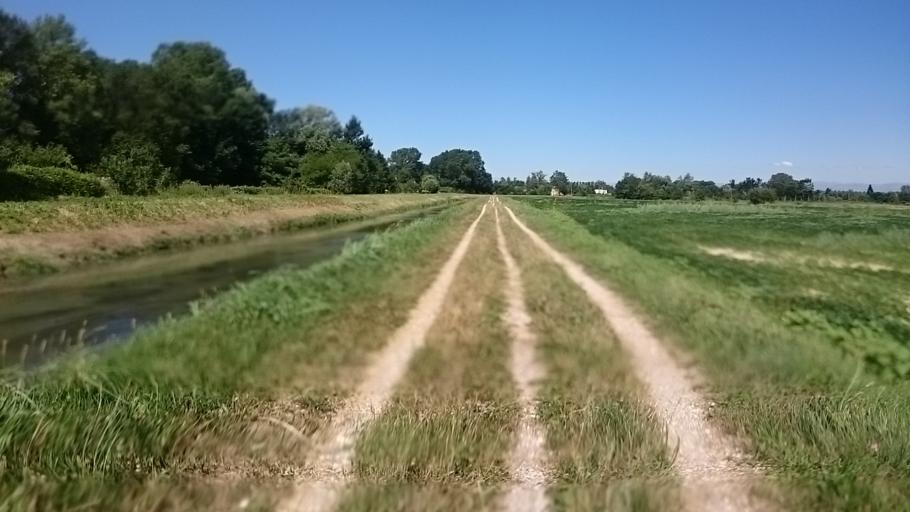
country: IT
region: Veneto
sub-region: Provincia di Padova
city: Vigonza
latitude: 45.4467
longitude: 11.9596
